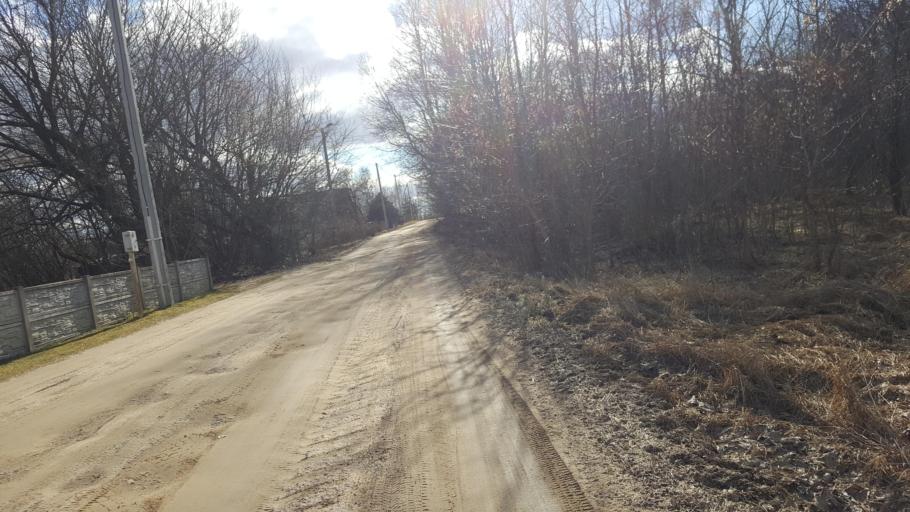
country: BY
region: Brest
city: Kamyanyets
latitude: 52.3908
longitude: 23.8843
